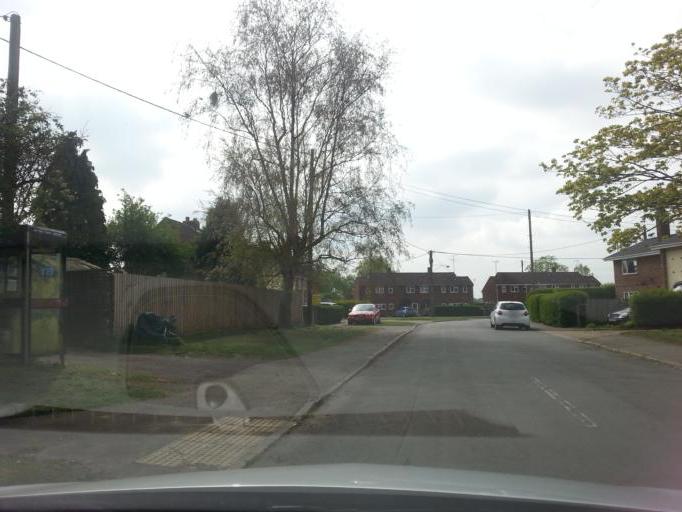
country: GB
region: England
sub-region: Norfolk
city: Outwell
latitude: 52.6065
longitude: 0.2363
